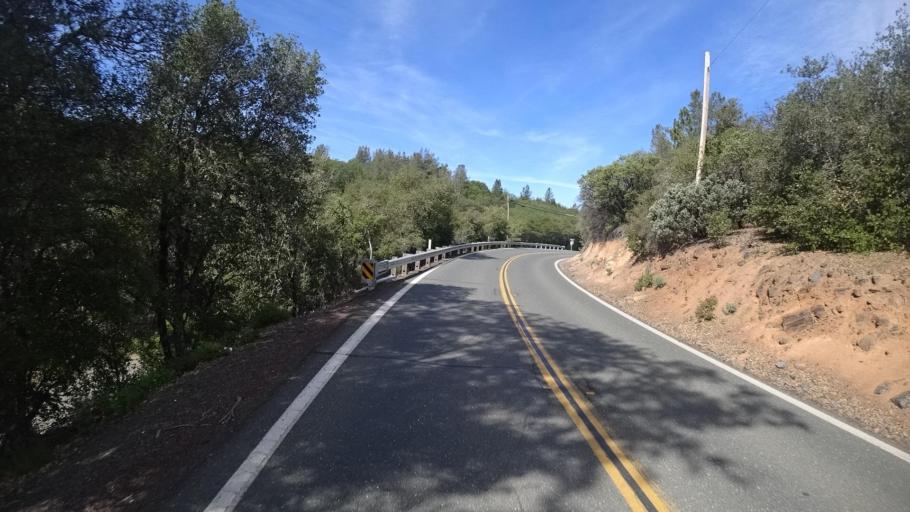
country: US
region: California
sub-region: Lake County
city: Cobb
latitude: 38.9078
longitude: -122.7630
